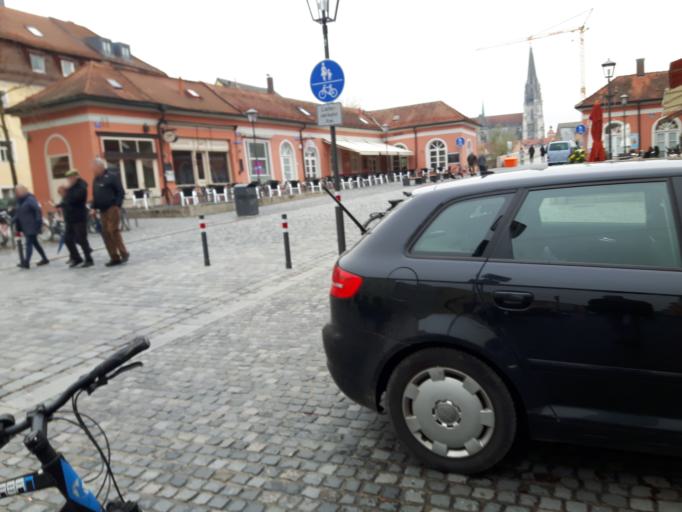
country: DE
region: Bavaria
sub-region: Upper Palatinate
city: Lappersdorf
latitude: 49.0245
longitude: 12.0973
